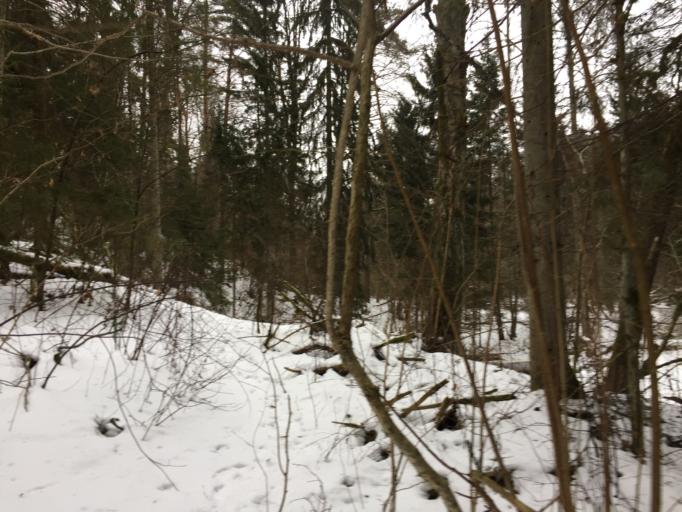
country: LV
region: Seja
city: Loja
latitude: 57.1482
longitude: 24.6820
